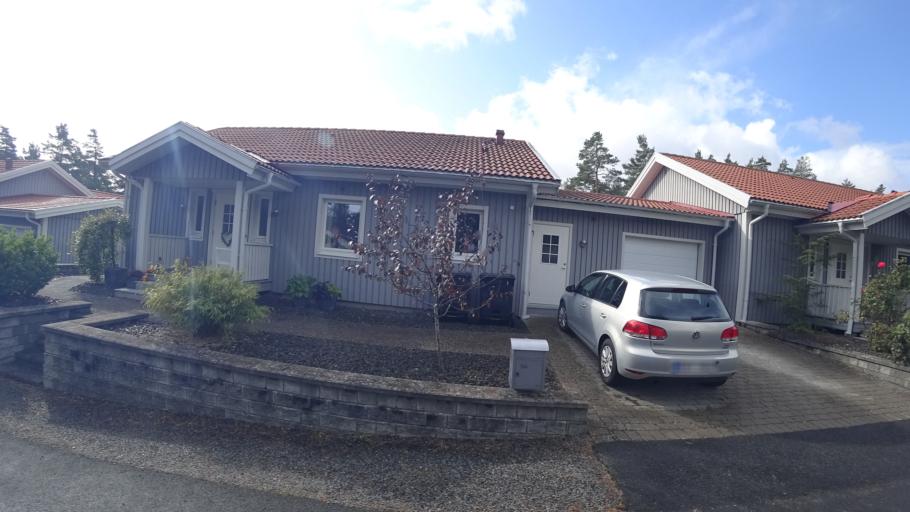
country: SE
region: Skane
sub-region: Kristianstads Kommun
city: Ahus
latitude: 55.9385
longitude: 14.3125
